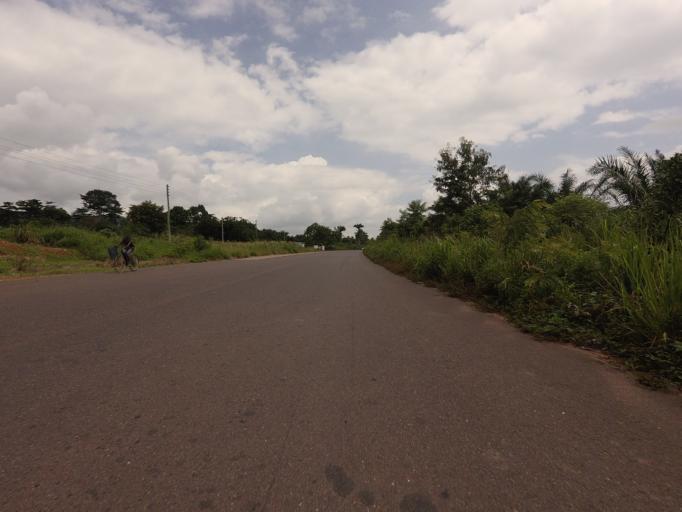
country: GH
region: Volta
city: Ho
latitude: 6.5439
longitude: 0.2495
